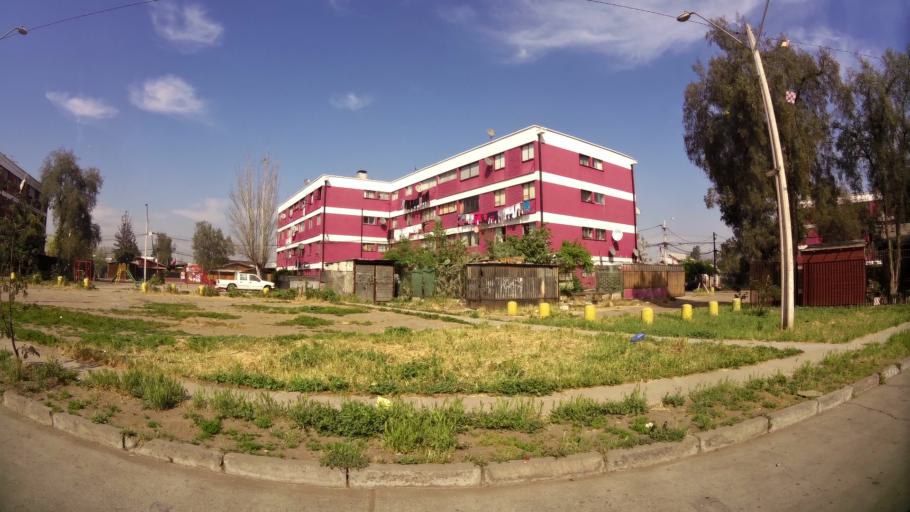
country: CL
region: Santiago Metropolitan
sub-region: Provincia de Santiago
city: Lo Prado
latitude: -33.4490
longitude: -70.7426
